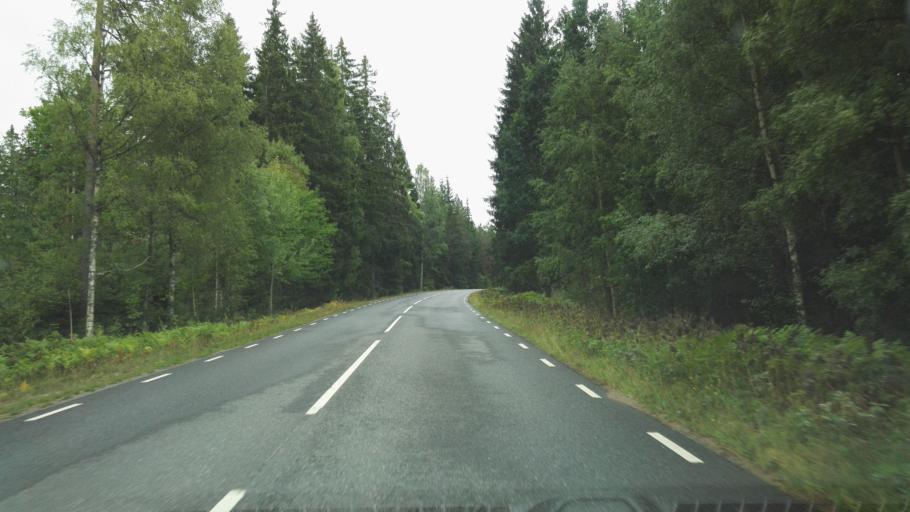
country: SE
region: Joenkoeping
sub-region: Vetlanda Kommun
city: Landsbro
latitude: 57.2520
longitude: 14.9440
